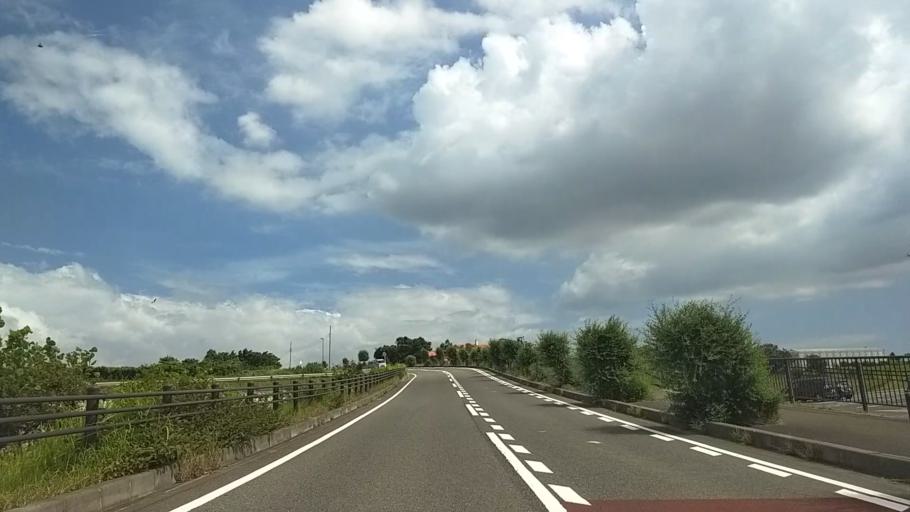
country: JP
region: Kanagawa
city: Miura
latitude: 35.1970
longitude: 139.6122
